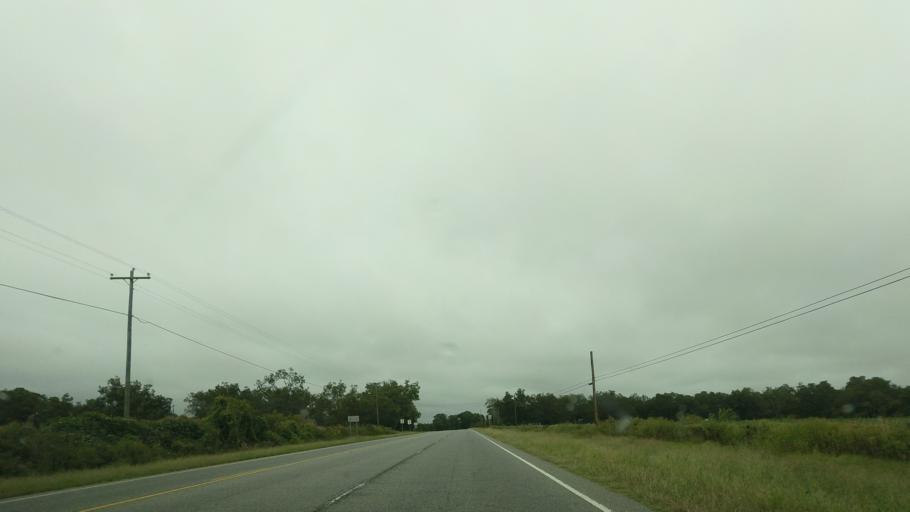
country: US
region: Georgia
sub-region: Irwin County
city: Ocilla
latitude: 31.6353
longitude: -83.2474
